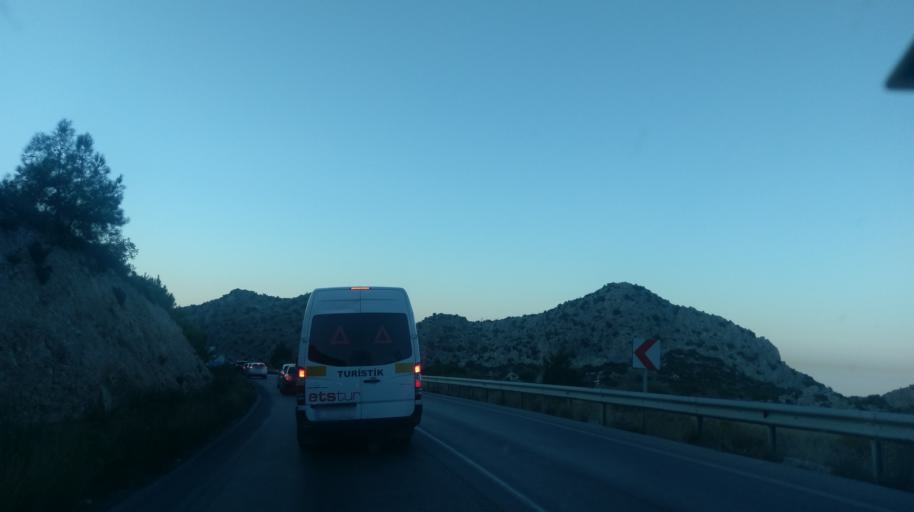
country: CY
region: Lefkosia
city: Nicosia
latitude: 35.2847
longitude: 33.4621
